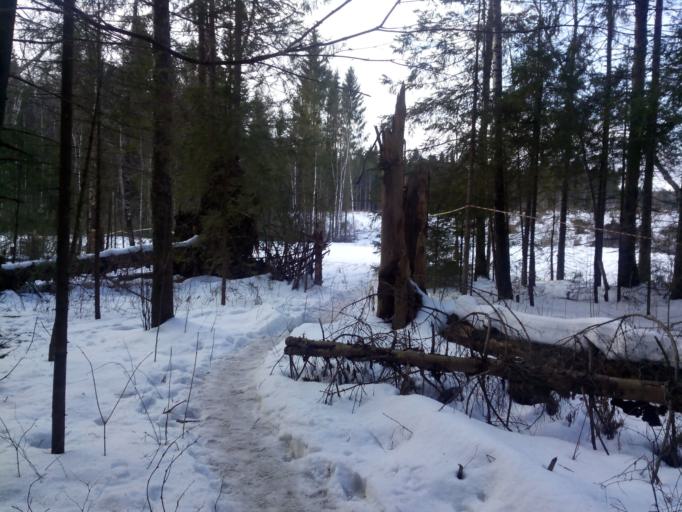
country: RU
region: Moskovskaya
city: Khot'kovo
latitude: 56.2270
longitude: 38.0313
